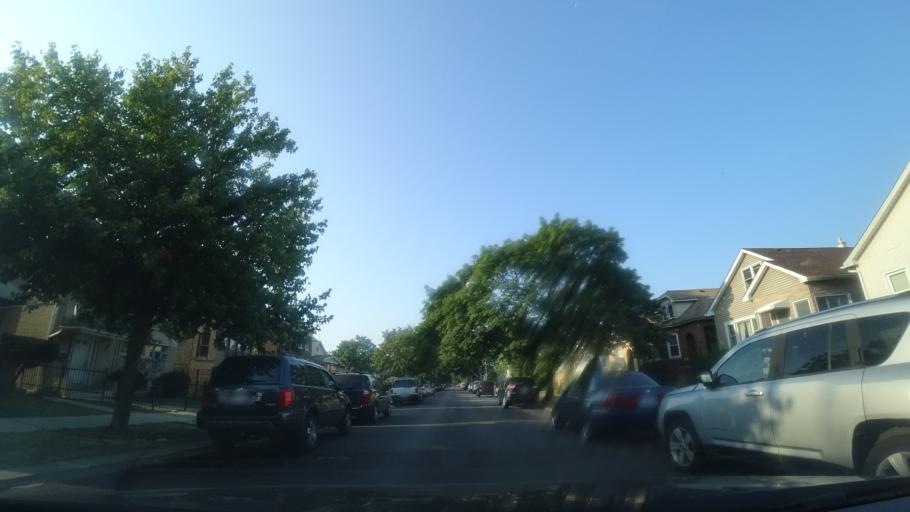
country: US
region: Illinois
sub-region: Cook County
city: Elmwood Park
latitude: 41.9227
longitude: -87.7782
